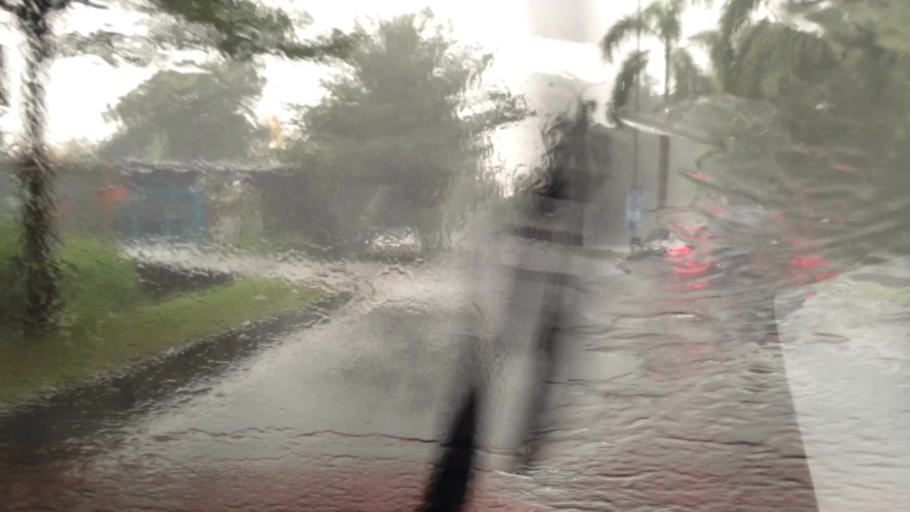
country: MY
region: Selangor
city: Subang Jaya
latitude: 3.0301
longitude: 101.5893
